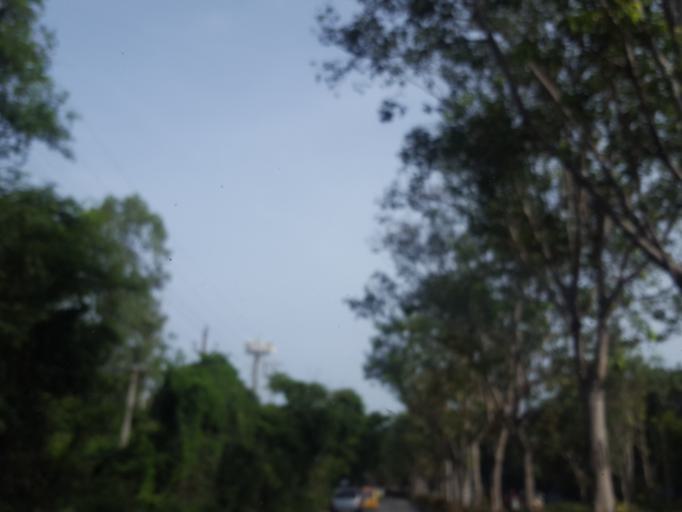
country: IN
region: Telangana
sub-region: Medak
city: Serilingampalle
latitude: 17.4640
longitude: 78.3344
